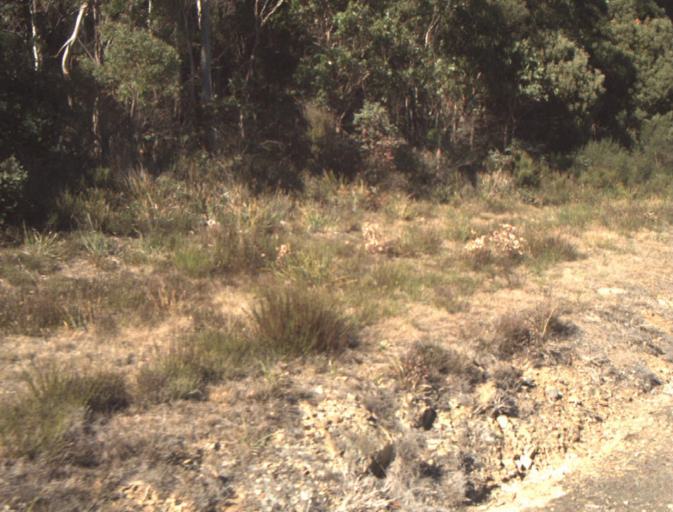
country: AU
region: Tasmania
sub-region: Launceston
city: Newstead
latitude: -41.3190
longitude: 147.3255
